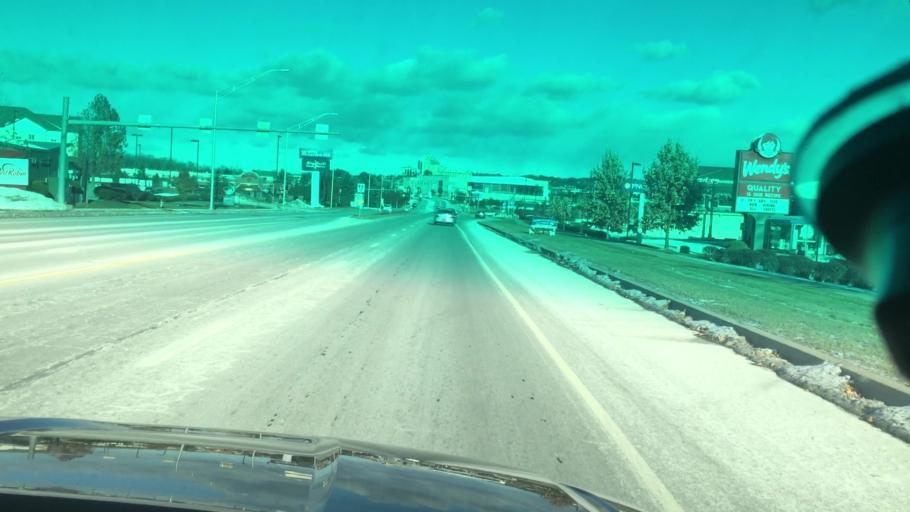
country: US
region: Pennsylvania
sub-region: Luzerne County
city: Georgetown
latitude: 41.2366
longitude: -75.8563
